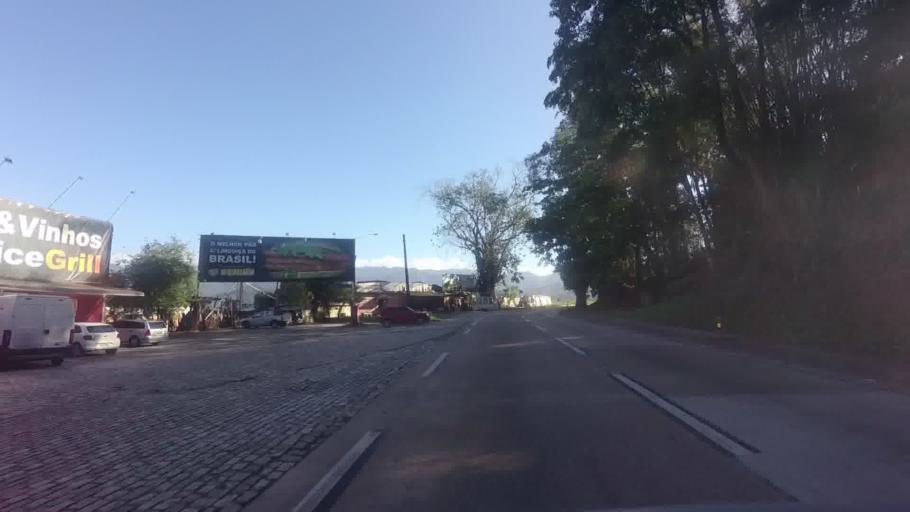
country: BR
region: Rio de Janeiro
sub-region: Petropolis
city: Petropolis
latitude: -22.5928
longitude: -43.2778
